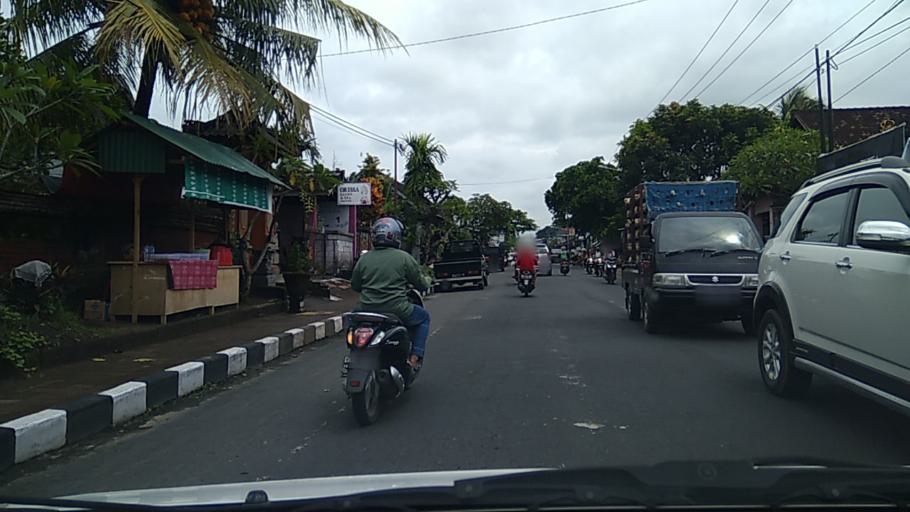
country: ID
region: Bali
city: Banjar Kembangsari
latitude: -8.5166
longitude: 115.2098
